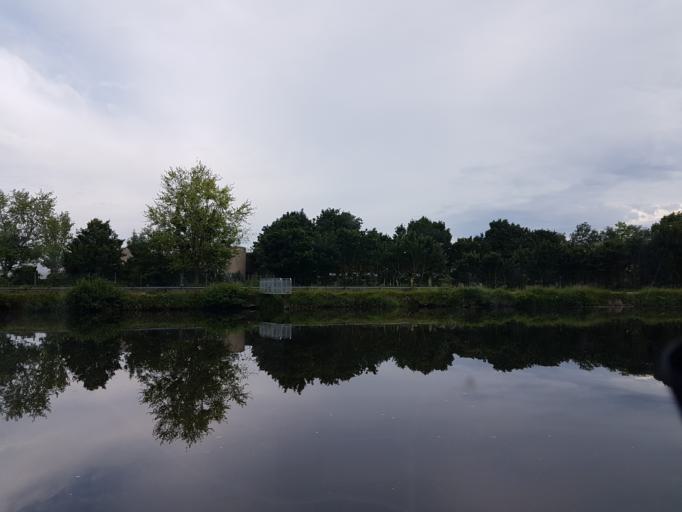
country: FR
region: Bourgogne
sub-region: Departement de l'Yonne
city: Auxerre
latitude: 47.8192
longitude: 3.5767
